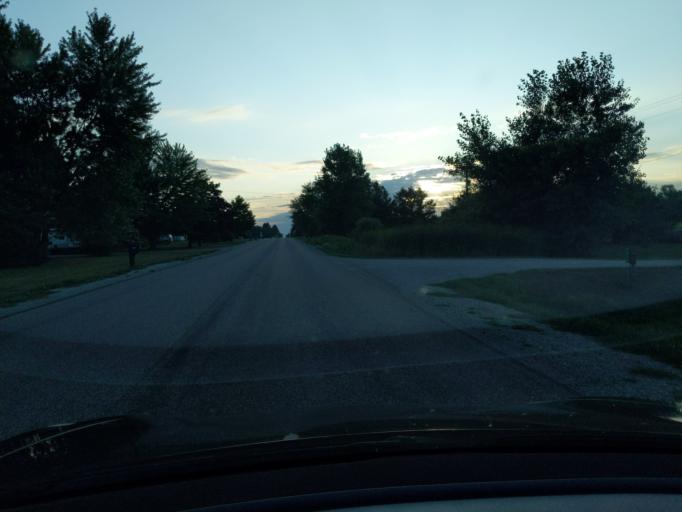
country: US
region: Michigan
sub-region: Gratiot County
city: Saint Louis
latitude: 43.3788
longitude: -84.5751
